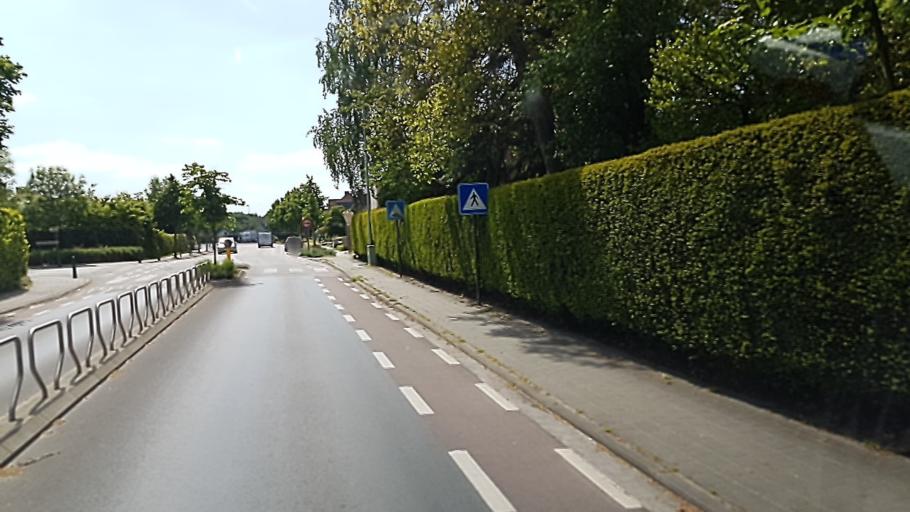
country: BE
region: Flanders
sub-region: Provincie West-Vlaanderen
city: Wevelgem
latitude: 50.8393
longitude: 3.2018
